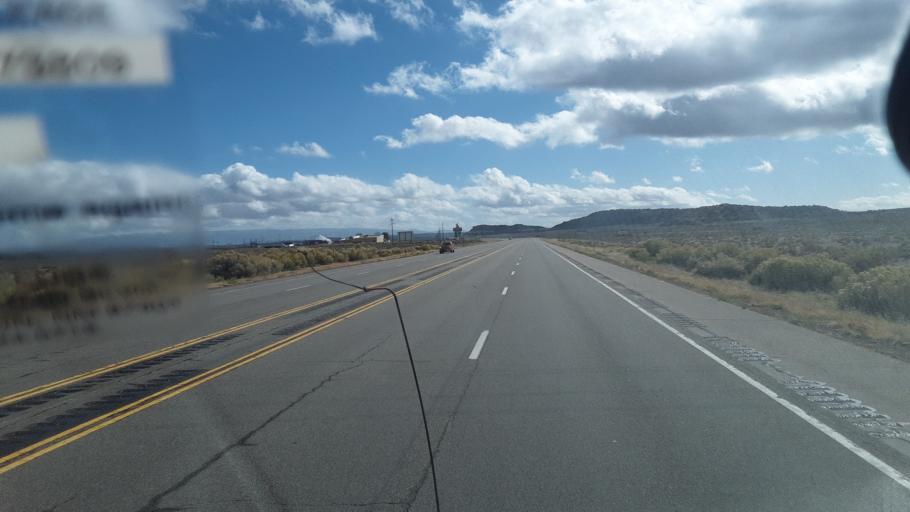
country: US
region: New Mexico
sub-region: Rio Arriba County
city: Santa Teresa
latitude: 36.1494
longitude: -107.2719
